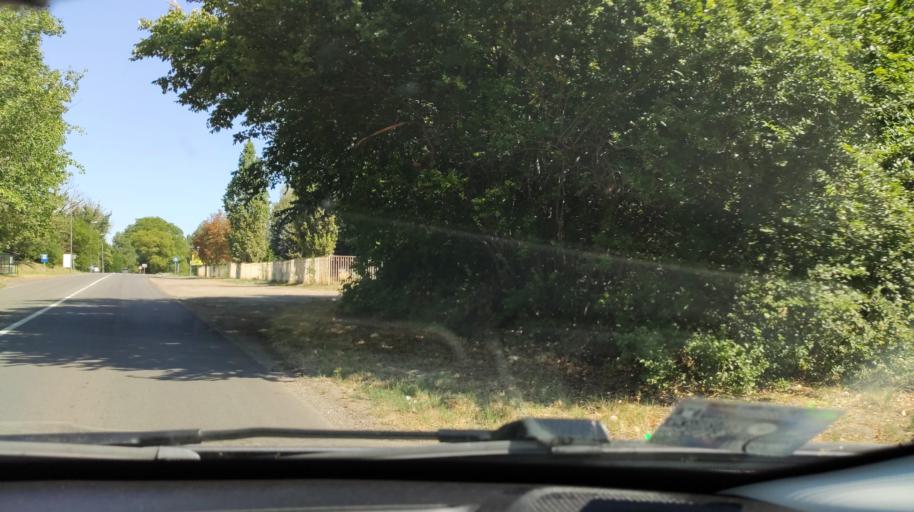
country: RS
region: Autonomna Pokrajina Vojvodina
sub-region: Severnobacki Okrug
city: Backa Topola
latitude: 45.8274
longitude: 19.6313
